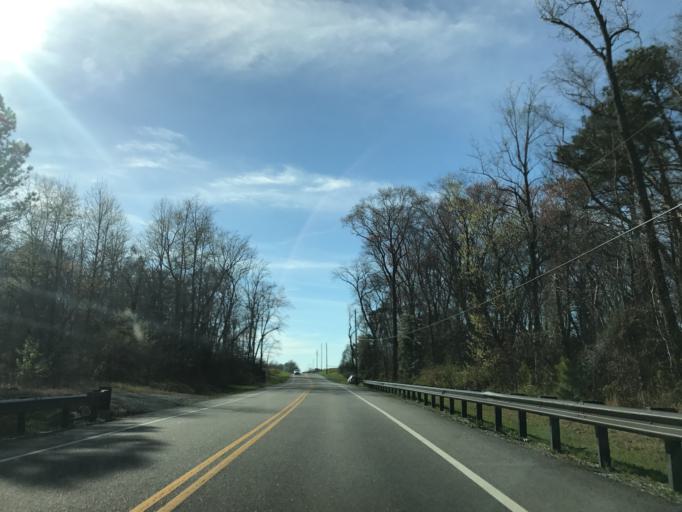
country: US
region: Maryland
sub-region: Caroline County
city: Greensboro
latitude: 39.0310
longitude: -75.7602
